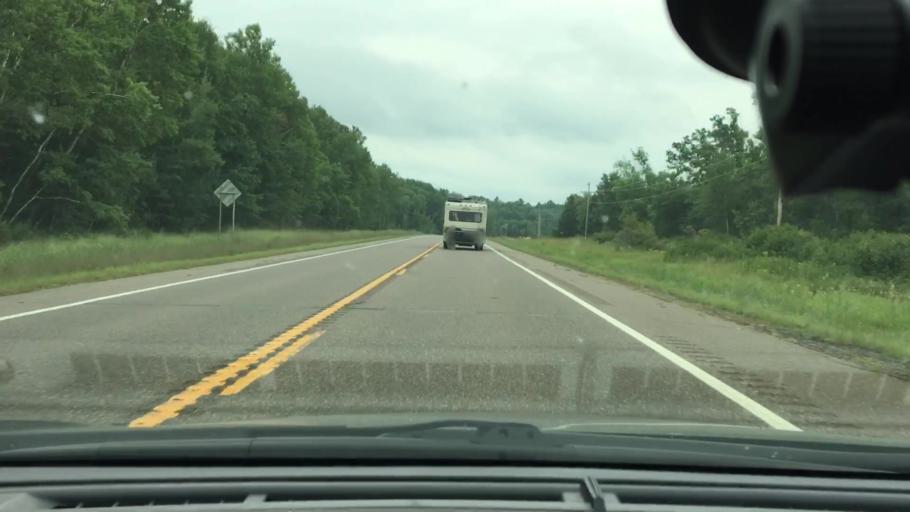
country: US
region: Minnesota
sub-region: Crow Wing County
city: Crosby
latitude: 46.5069
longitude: -93.9593
